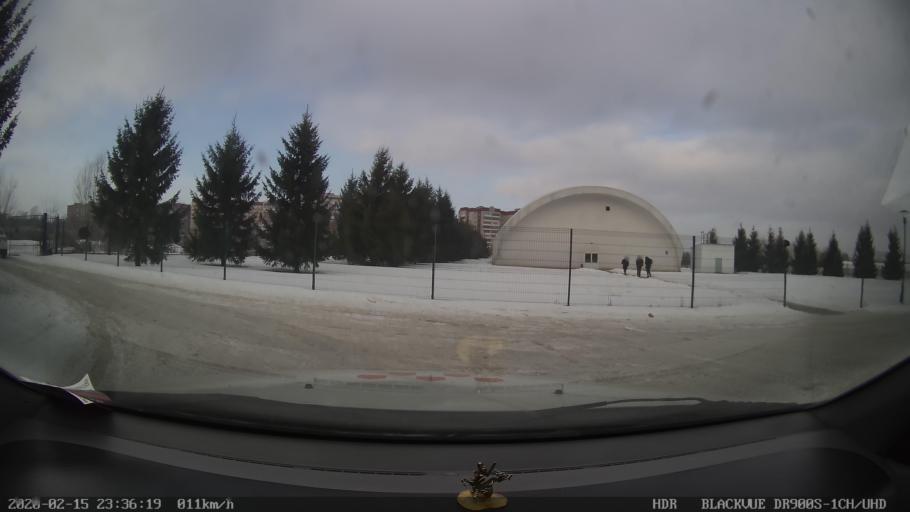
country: RU
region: Tatarstan
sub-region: Gorod Kazan'
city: Kazan
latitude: 55.7925
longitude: 49.1937
